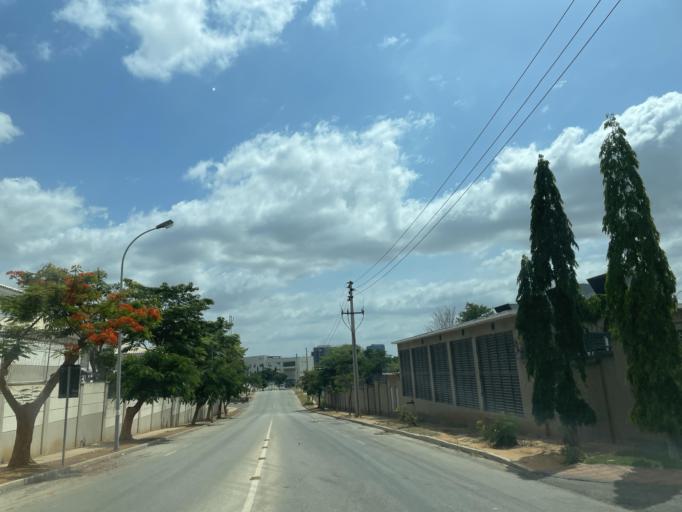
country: AO
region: Luanda
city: Luanda
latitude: -8.9315
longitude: 13.1843
